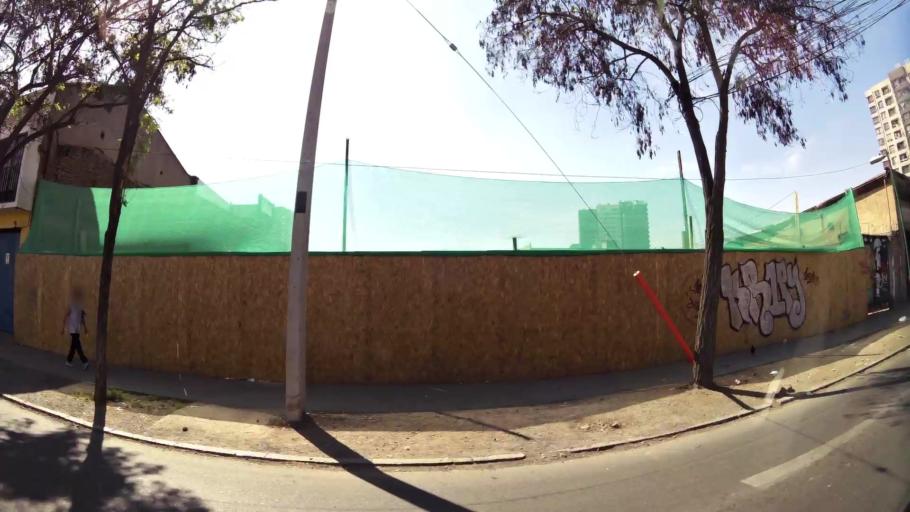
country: CL
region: Santiago Metropolitan
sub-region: Provincia de Santiago
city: Santiago
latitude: -33.4225
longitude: -70.6580
